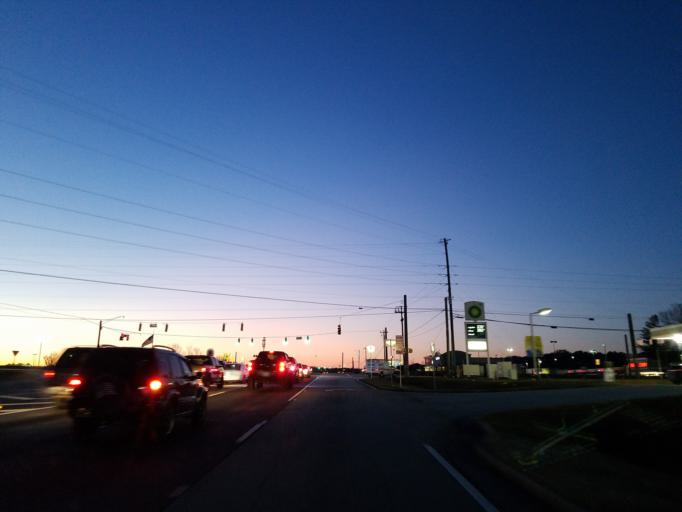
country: US
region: Georgia
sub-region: Paulding County
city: Hiram
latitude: 33.8914
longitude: -84.7539
